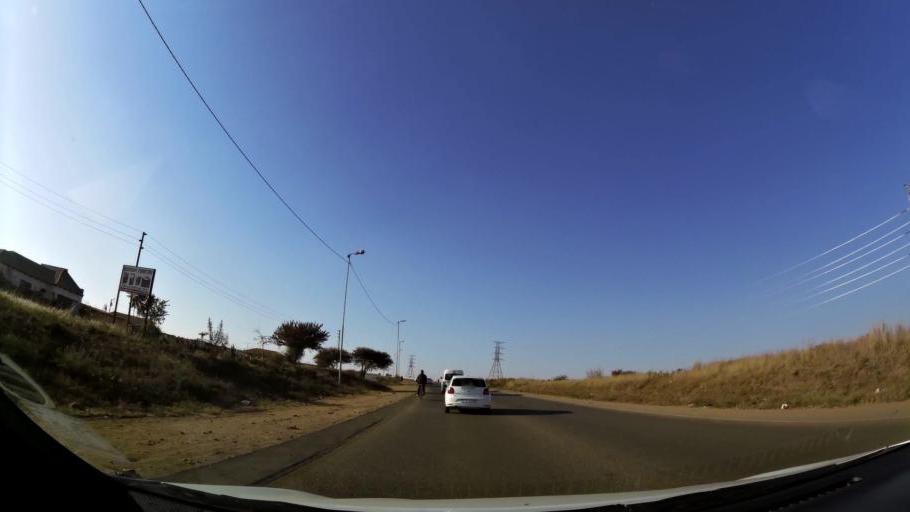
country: ZA
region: Gauteng
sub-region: City of Tshwane Metropolitan Municipality
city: Cullinan
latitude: -25.7328
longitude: 28.3980
